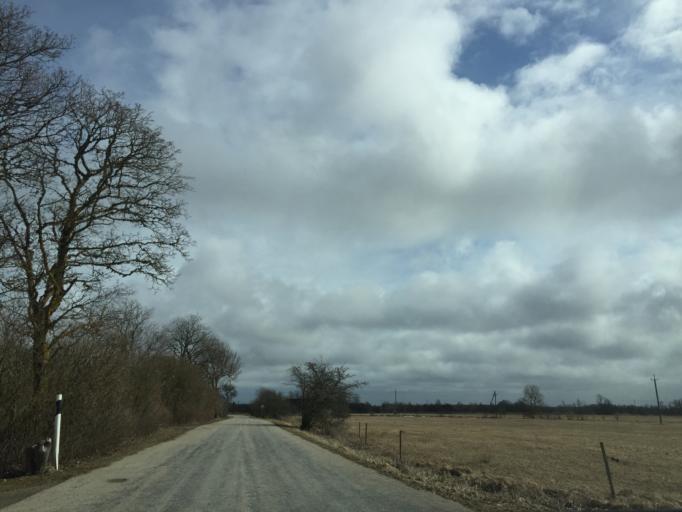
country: EE
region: Laeaene
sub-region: Lihula vald
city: Lihula
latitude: 58.7350
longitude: 23.8454
